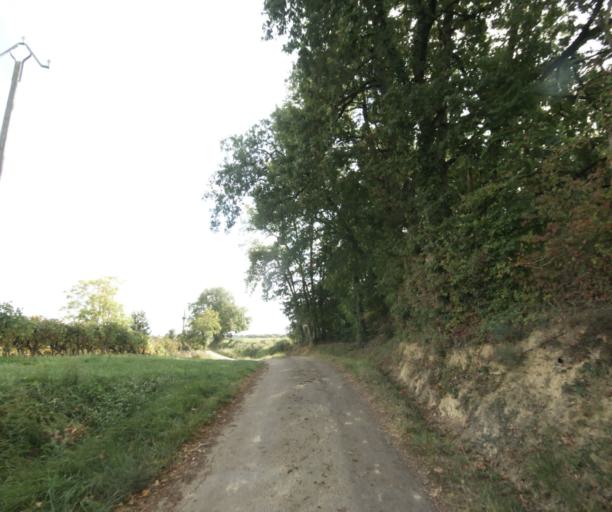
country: FR
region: Midi-Pyrenees
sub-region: Departement du Gers
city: Gondrin
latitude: 43.8551
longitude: 0.2724
